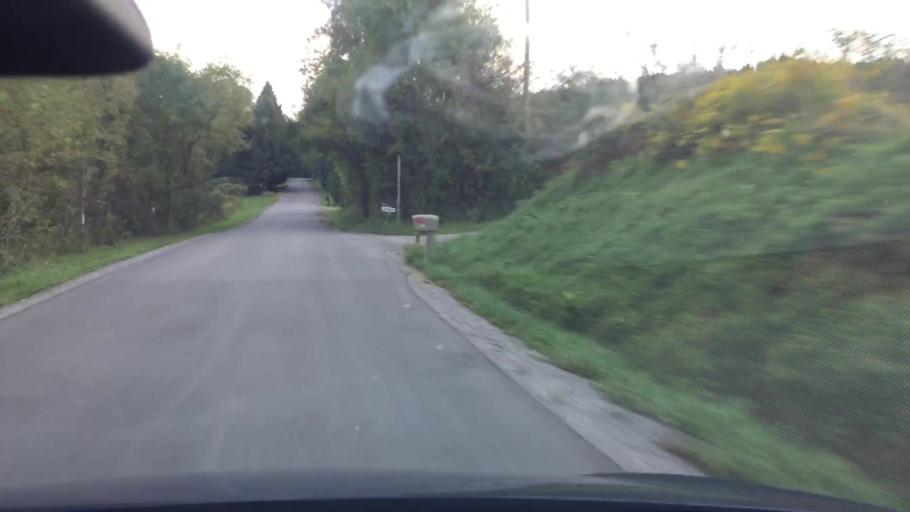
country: US
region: Pennsylvania
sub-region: Butler County
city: Oak Hills
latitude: 40.8000
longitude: -79.8870
